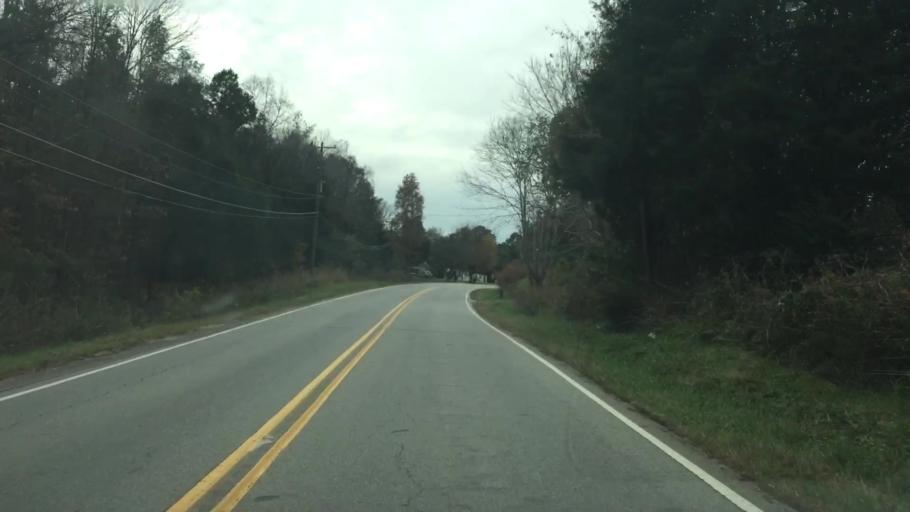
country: US
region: North Carolina
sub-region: Rowan County
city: China Grove
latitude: 35.6500
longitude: -80.6104
